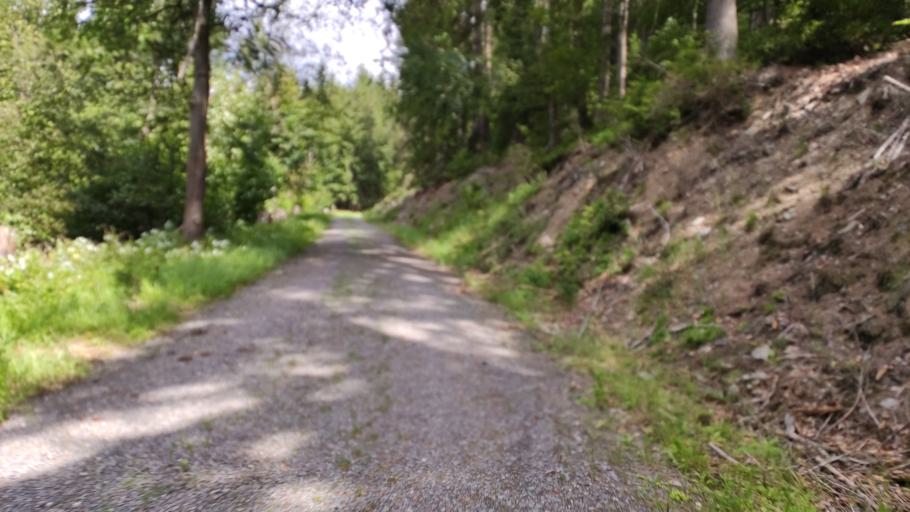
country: DE
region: Bavaria
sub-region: Upper Franconia
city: Tschirn
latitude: 50.3859
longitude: 11.4685
